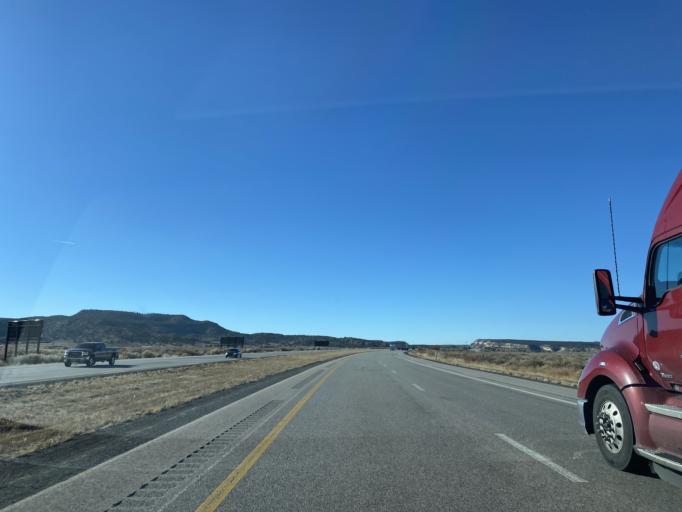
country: US
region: New Mexico
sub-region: McKinley County
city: Gallup
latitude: 35.4429
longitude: -108.9584
